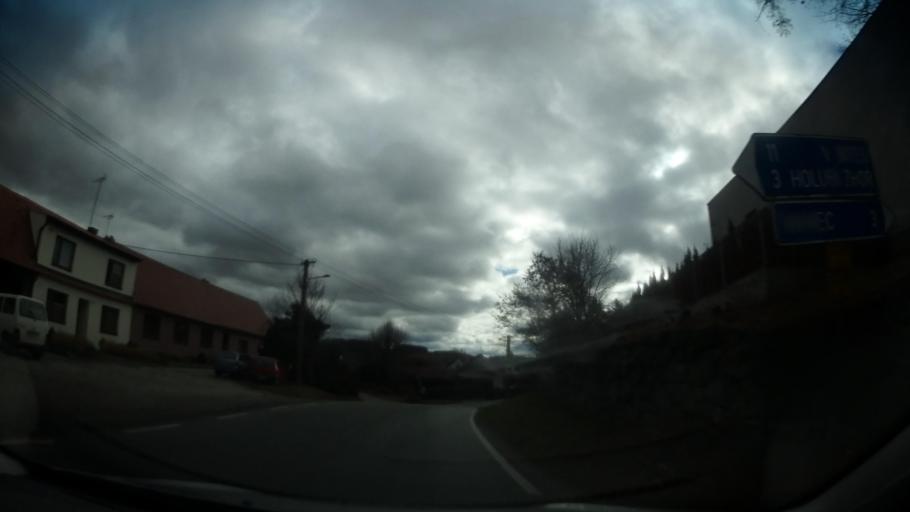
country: CZ
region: Vysocina
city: Budisov
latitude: 49.2862
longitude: 16.0977
